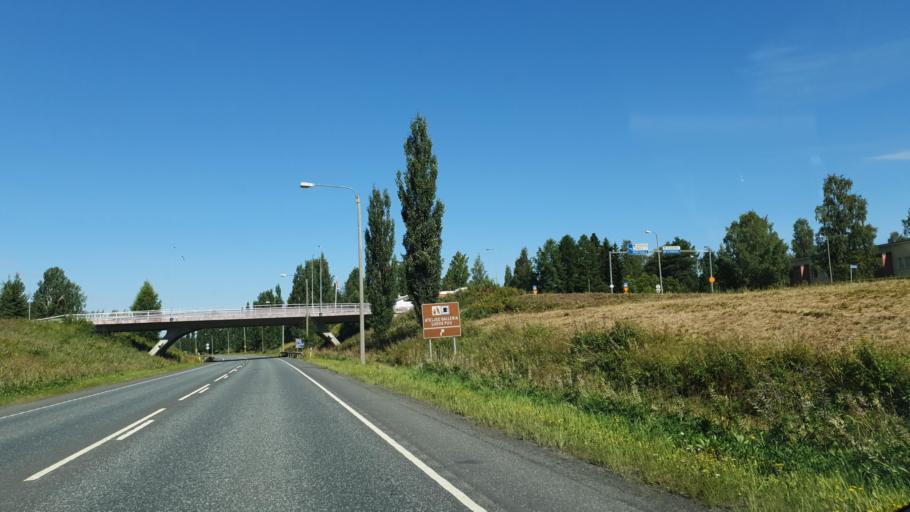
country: FI
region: Northern Savo
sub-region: Ylae-Savo
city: Lapinlahti
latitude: 63.3656
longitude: 27.4073
